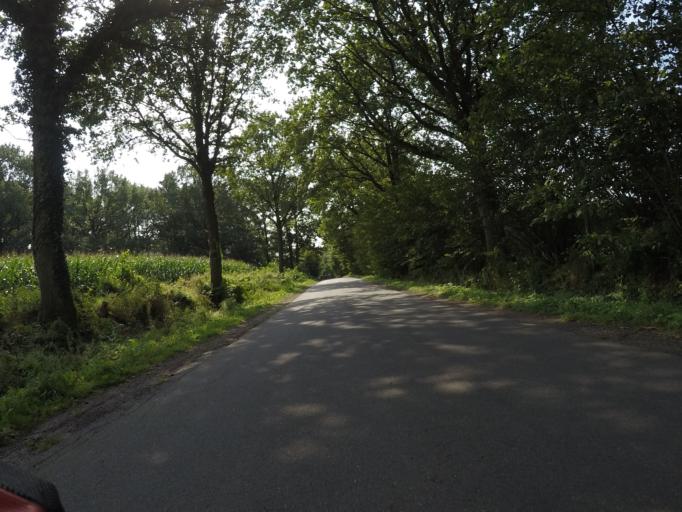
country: DE
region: Schleswig-Holstein
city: Kisdorf
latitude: 53.7733
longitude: 10.0194
